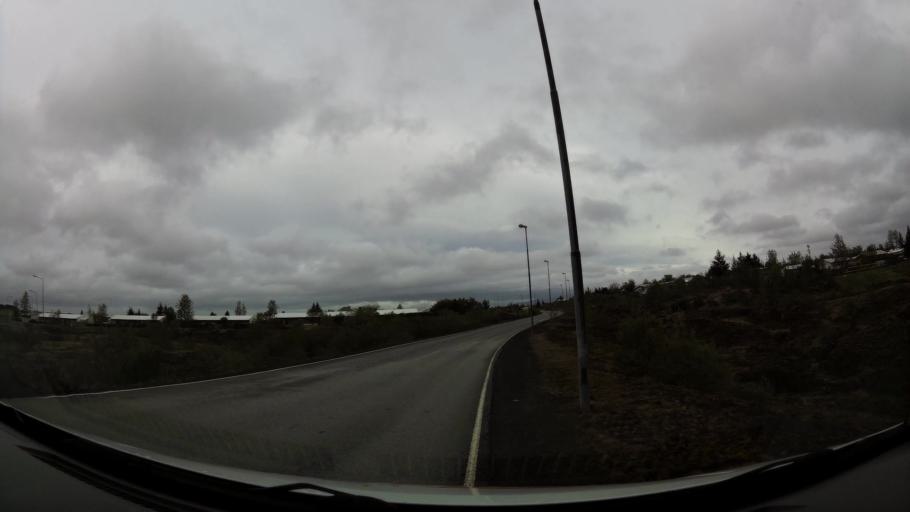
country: IS
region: Capital Region
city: Hafnarfjoerdur
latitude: 64.0800
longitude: -21.9712
